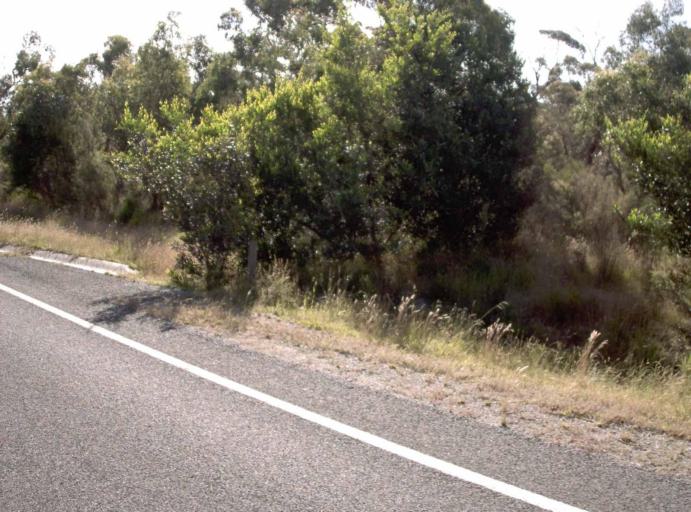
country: AU
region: Victoria
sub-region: Bass Coast
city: North Wonthaggi
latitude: -38.4376
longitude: 145.4884
